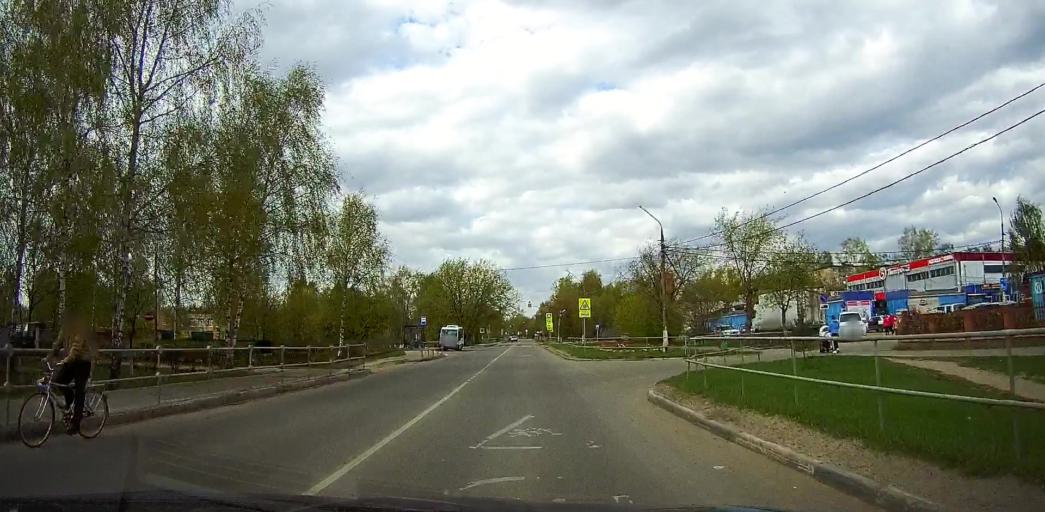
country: RU
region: Moskovskaya
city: Pavlovskiy Posad
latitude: 55.7668
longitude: 38.6559
